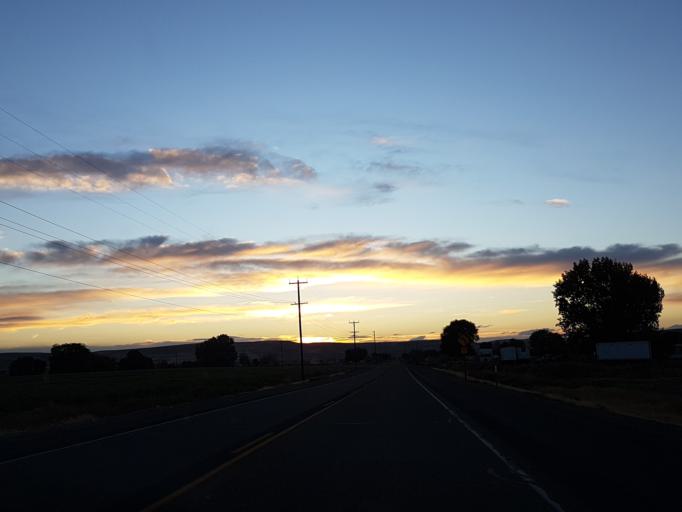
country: US
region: Oregon
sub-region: Malheur County
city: Vale
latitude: 43.9395
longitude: -117.3678
